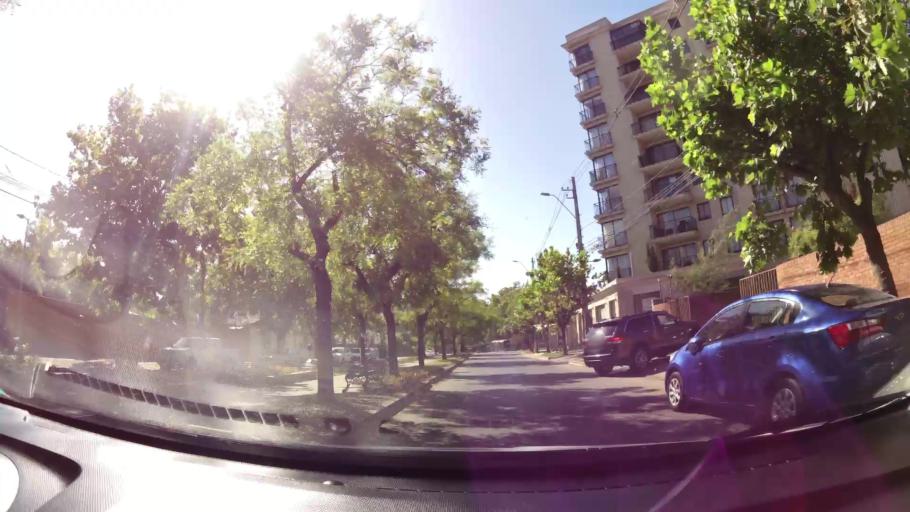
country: CL
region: Maule
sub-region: Provincia de Talca
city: Talca
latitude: -35.4224
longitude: -71.6699
